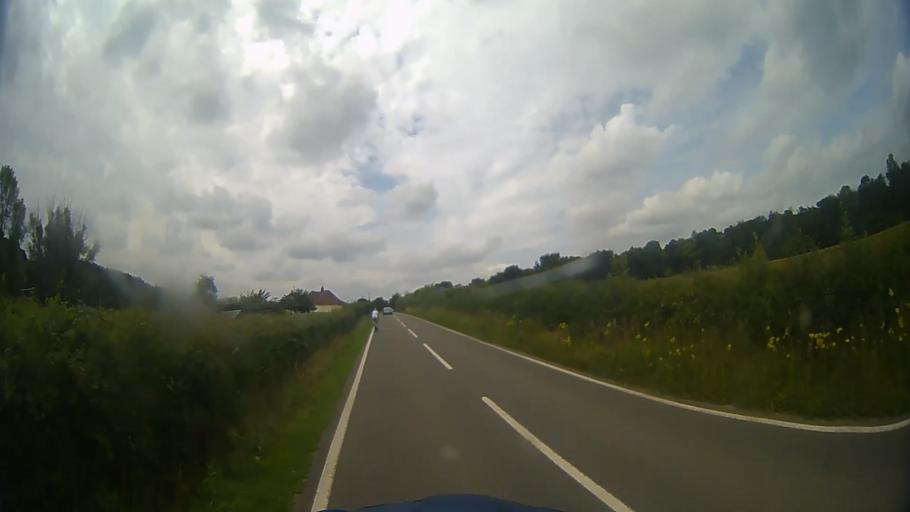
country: GB
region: England
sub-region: Hampshire
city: Kingsley
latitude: 51.1732
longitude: -0.8659
